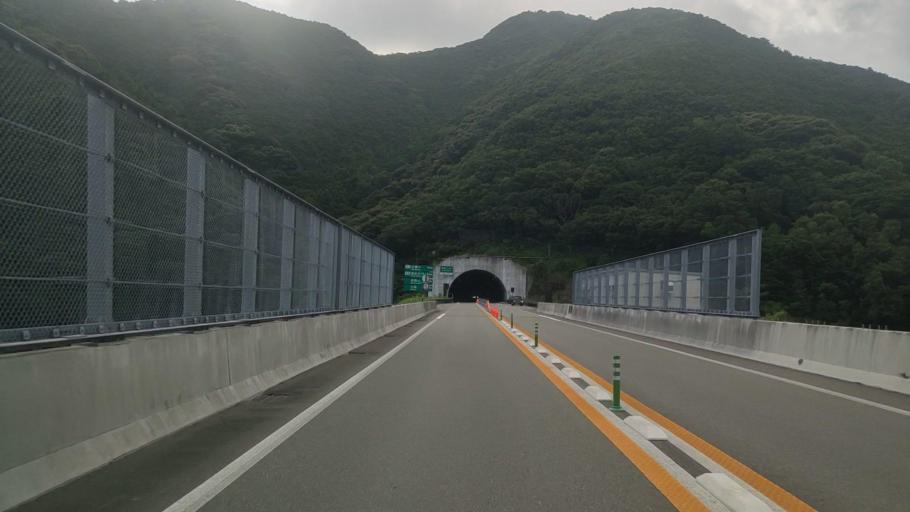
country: JP
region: Wakayama
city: Tanabe
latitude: 33.5661
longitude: 135.4939
